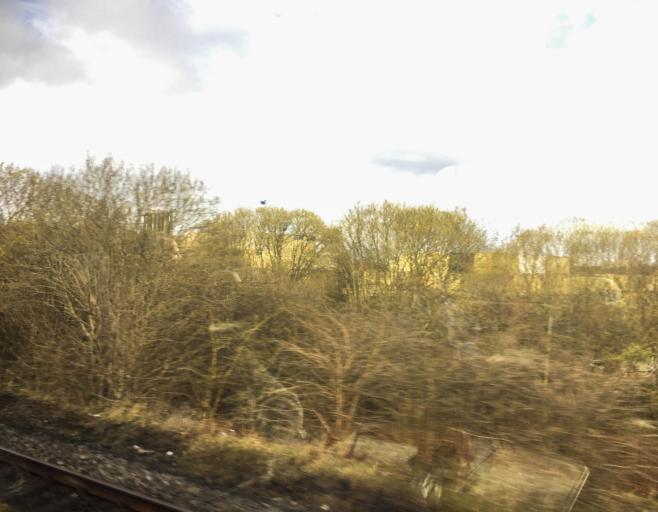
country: GB
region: Scotland
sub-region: North Lanarkshire
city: Coatbridge
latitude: 55.8702
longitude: -4.0376
